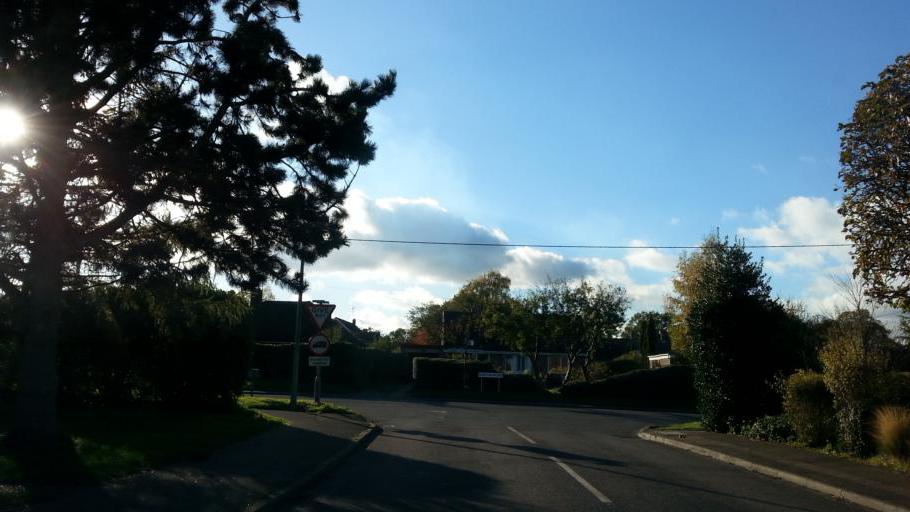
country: GB
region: England
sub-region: Suffolk
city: Thurston
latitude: 52.2528
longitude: 0.8064
